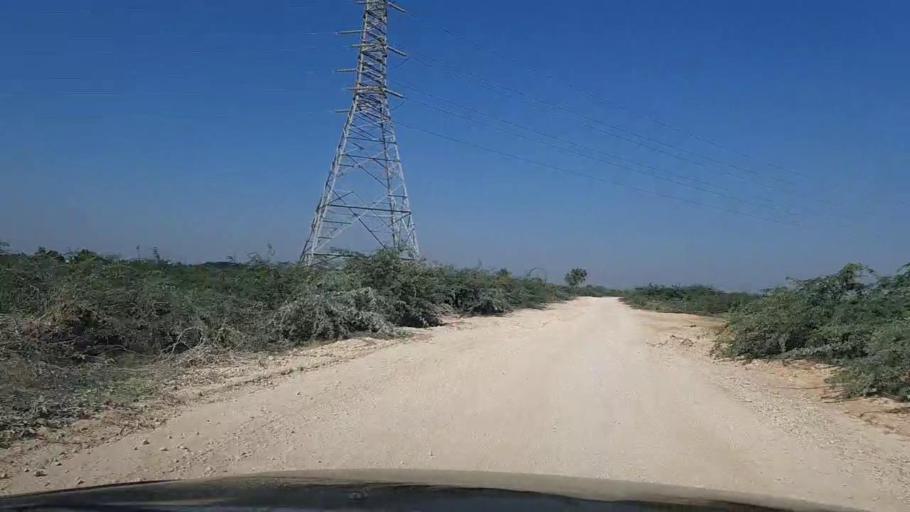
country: PK
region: Sindh
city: Thatta
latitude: 24.6242
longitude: 67.8360
